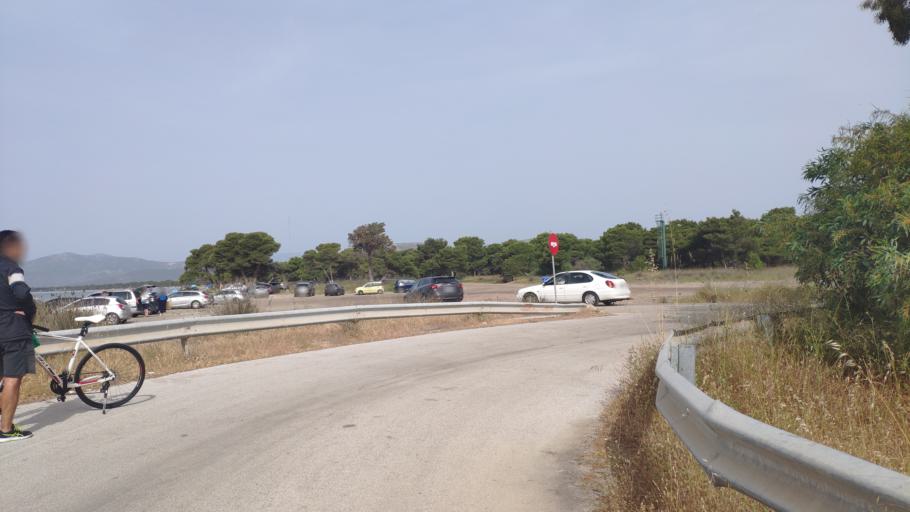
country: GR
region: Attica
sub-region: Nomarchia Anatolikis Attikis
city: Kato Soulion
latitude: 38.1432
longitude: 24.0511
